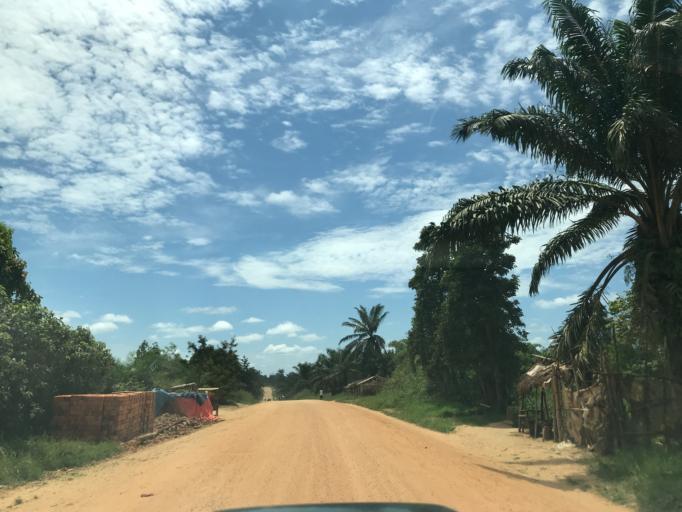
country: CD
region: Eastern Province
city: Kisangani
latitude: 0.5652
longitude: 25.1875
